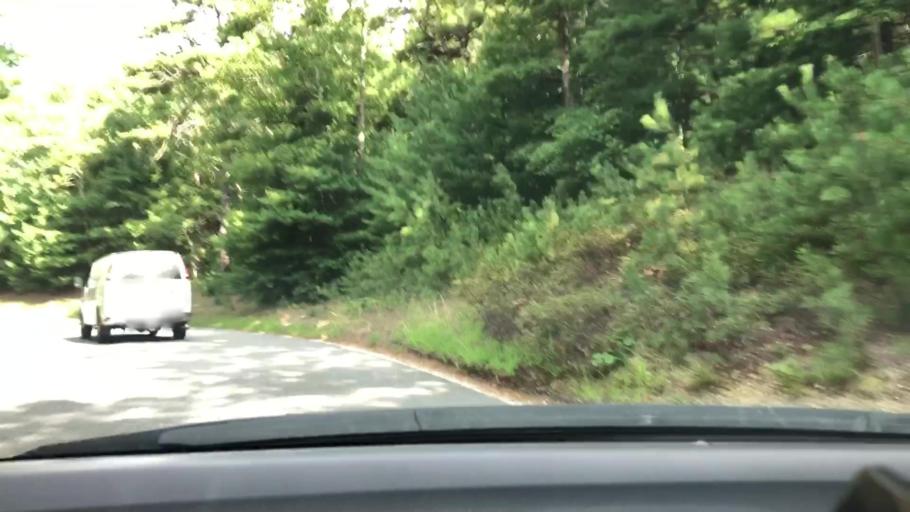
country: US
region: Massachusetts
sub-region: Plymouth County
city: White Island Shores
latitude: 41.8907
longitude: -70.5840
